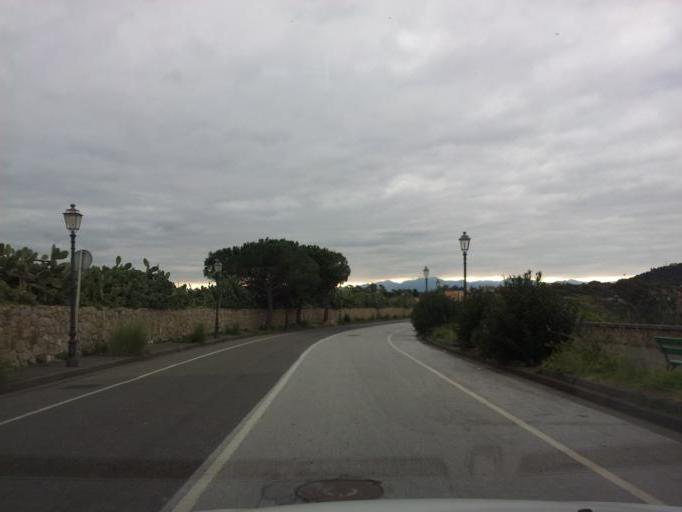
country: IT
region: Sicily
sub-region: Messina
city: Milazzo
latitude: 38.2668
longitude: 15.2364
